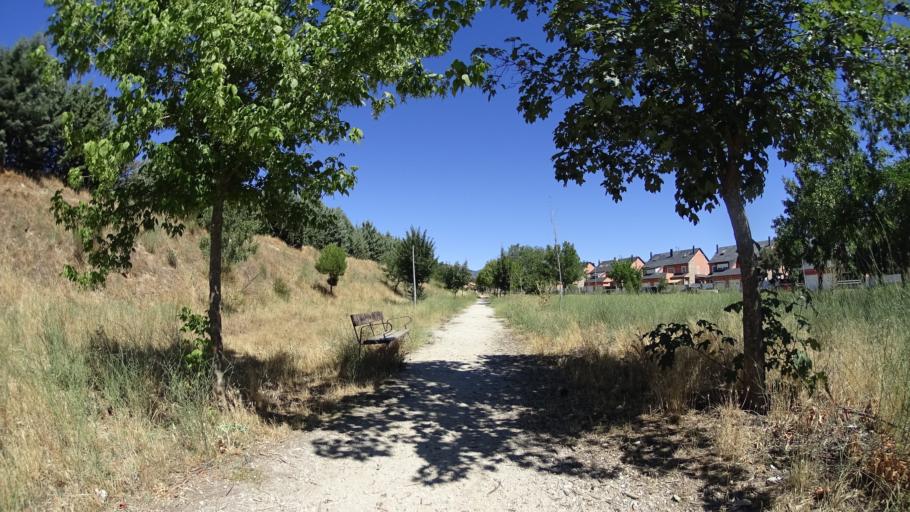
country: ES
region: Madrid
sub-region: Provincia de Madrid
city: Alpedrete
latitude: 40.6447
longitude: -4.0252
